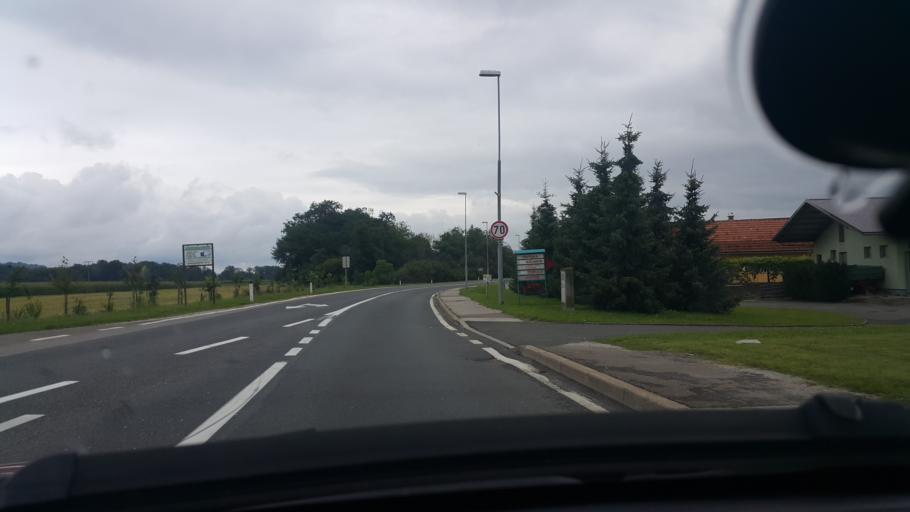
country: SI
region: Gorisnica
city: Gorisnica
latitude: 46.4166
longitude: 16.0001
